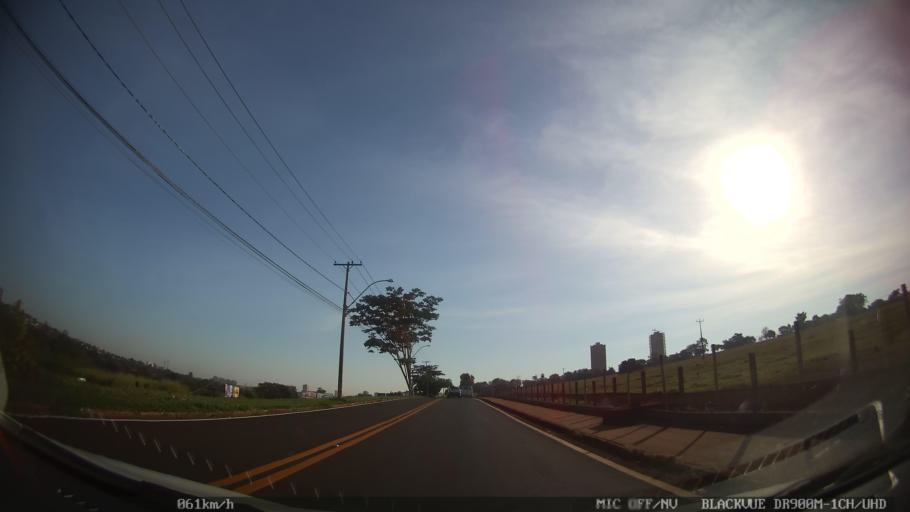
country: BR
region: Sao Paulo
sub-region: Ribeirao Preto
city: Ribeirao Preto
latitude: -21.2471
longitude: -47.8192
